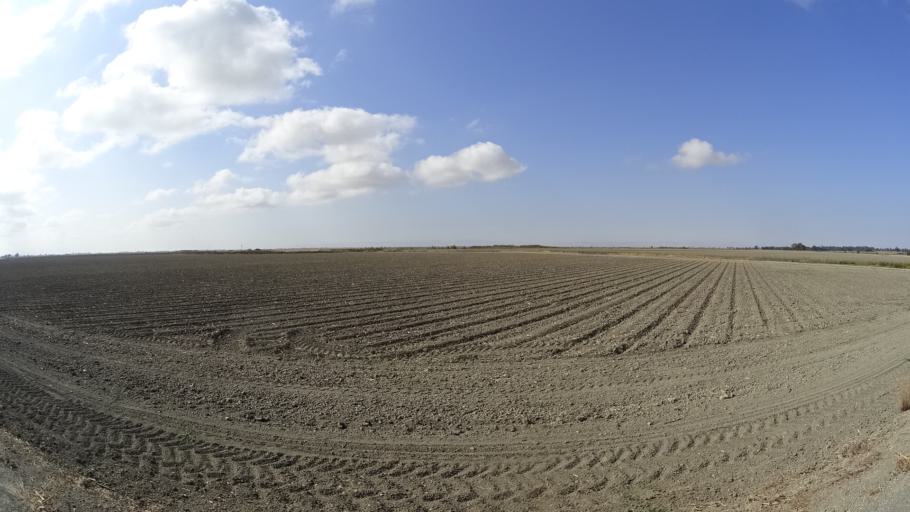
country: US
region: California
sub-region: Yolo County
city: Woodland
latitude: 38.8439
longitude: -121.7525
